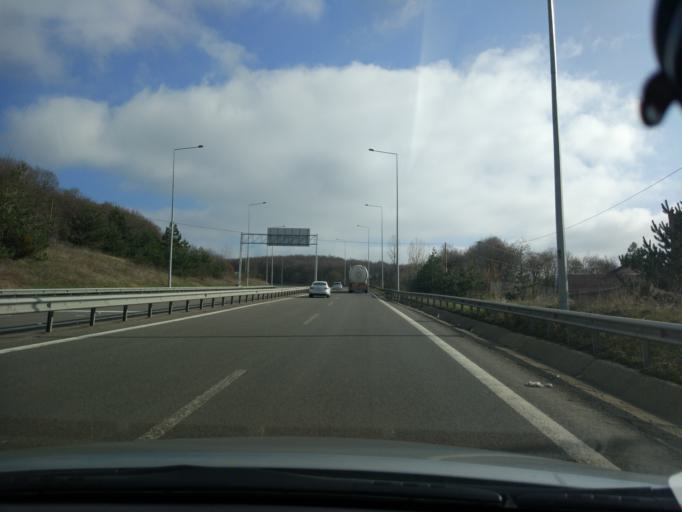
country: TR
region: Bolu
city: Bolu
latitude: 40.7183
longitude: 31.4734
